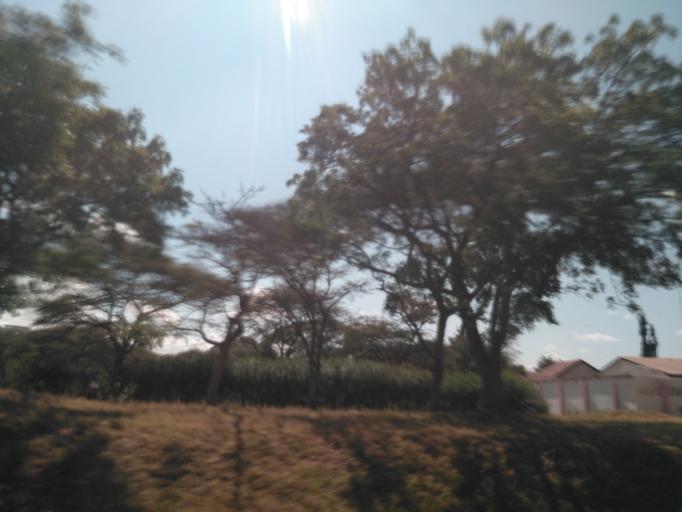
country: TZ
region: Dodoma
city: Dodoma
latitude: -6.1598
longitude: 35.7540
